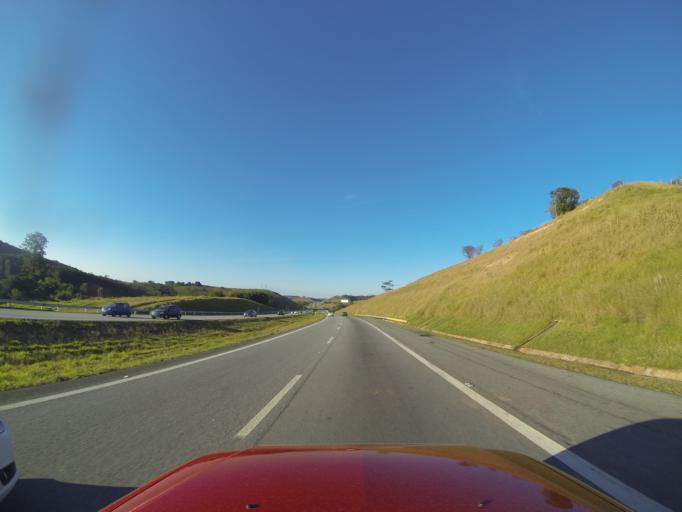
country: BR
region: Sao Paulo
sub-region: Jacarei
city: Jacarei
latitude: -23.3136
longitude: -45.8996
